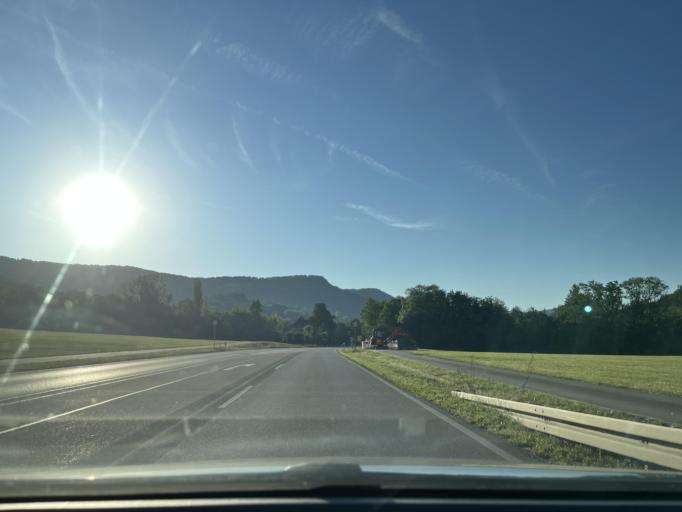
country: DE
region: Baden-Wuerttemberg
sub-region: Tuebingen Region
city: Jungingen
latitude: 48.3488
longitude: 9.0170
